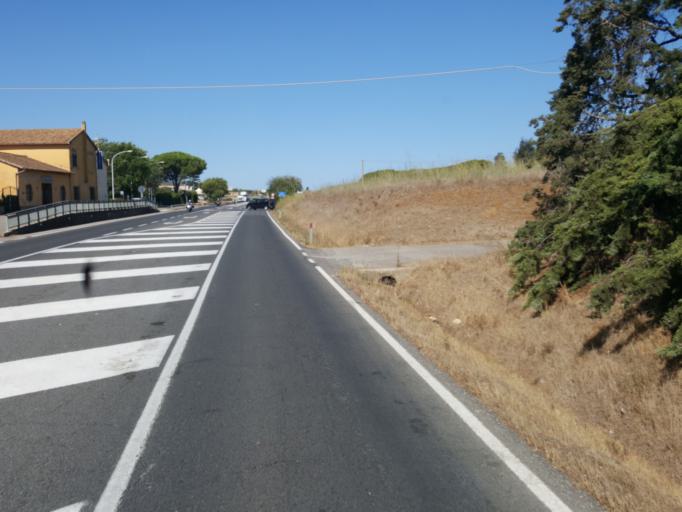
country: IT
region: Tuscany
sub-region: Provincia di Grosseto
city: Orbetello Scalo
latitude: 42.4148
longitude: 11.3279
